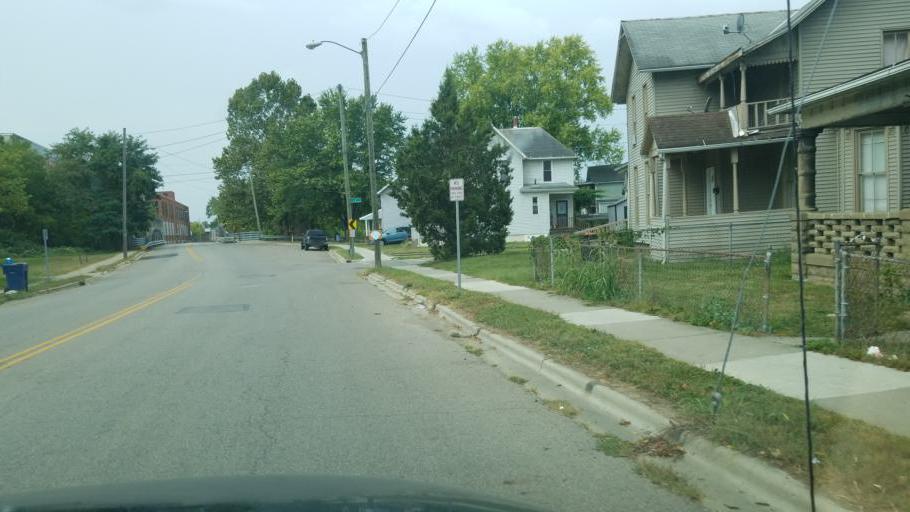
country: US
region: Ohio
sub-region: Licking County
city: Newark
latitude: 40.0557
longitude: -82.4114
